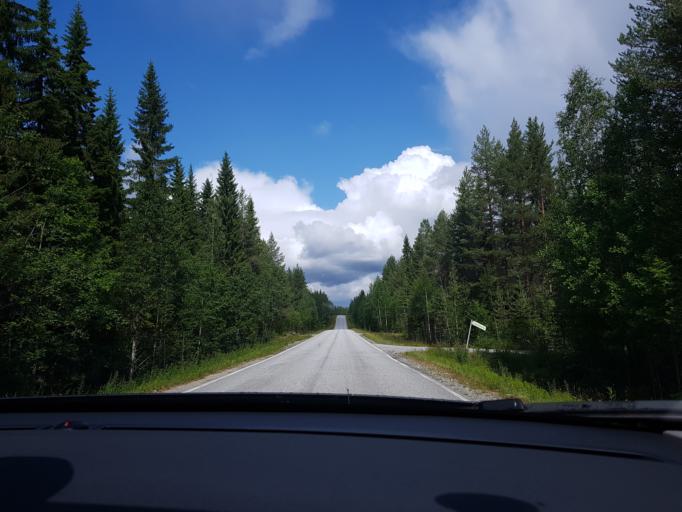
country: FI
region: Kainuu
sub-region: Kehys-Kainuu
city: Kuhmo
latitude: 64.4283
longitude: 29.4983
